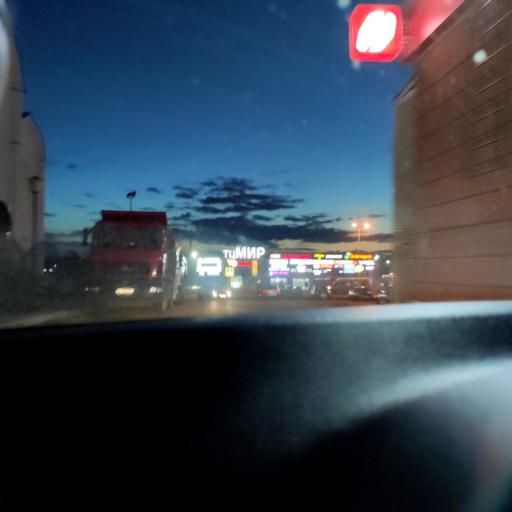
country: RU
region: Samara
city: Petra-Dubrava
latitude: 53.3167
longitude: 50.3051
